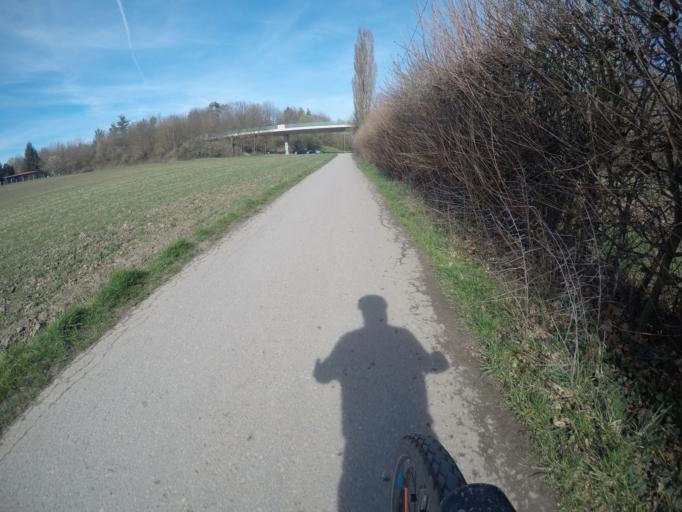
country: DE
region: Baden-Wuerttemberg
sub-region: Regierungsbezirk Stuttgart
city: Korntal
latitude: 48.8059
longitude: 9.1209
